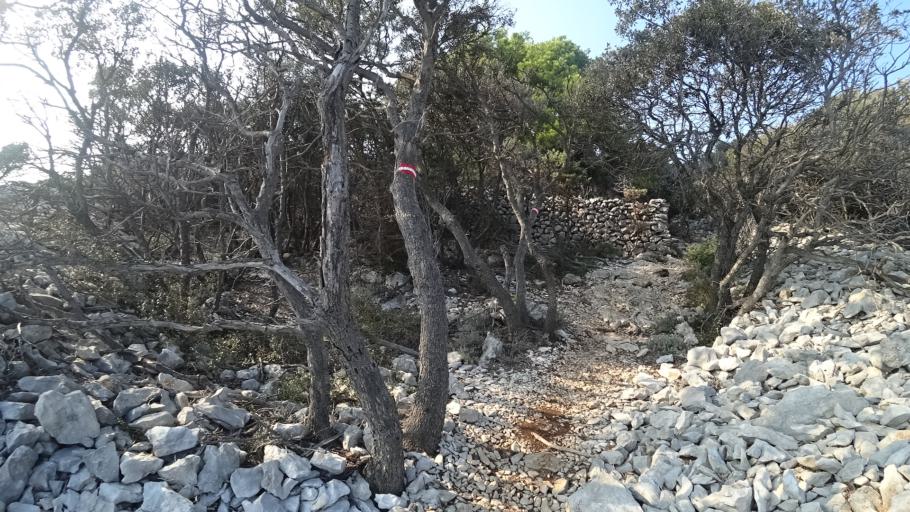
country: HR
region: Primorsko-Goranska
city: Mali Losinj
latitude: 44.5112
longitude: 14.4780
